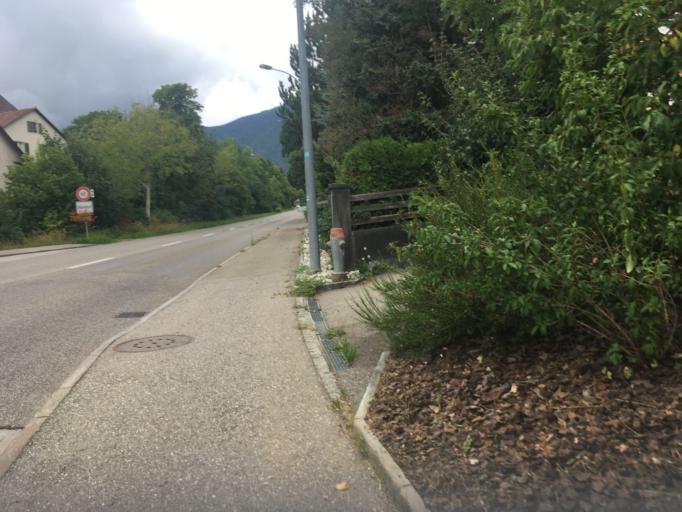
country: CH
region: Solothurn
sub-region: Bezirk Lebern
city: Langendorf
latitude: 47.2273
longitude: 7.5086
